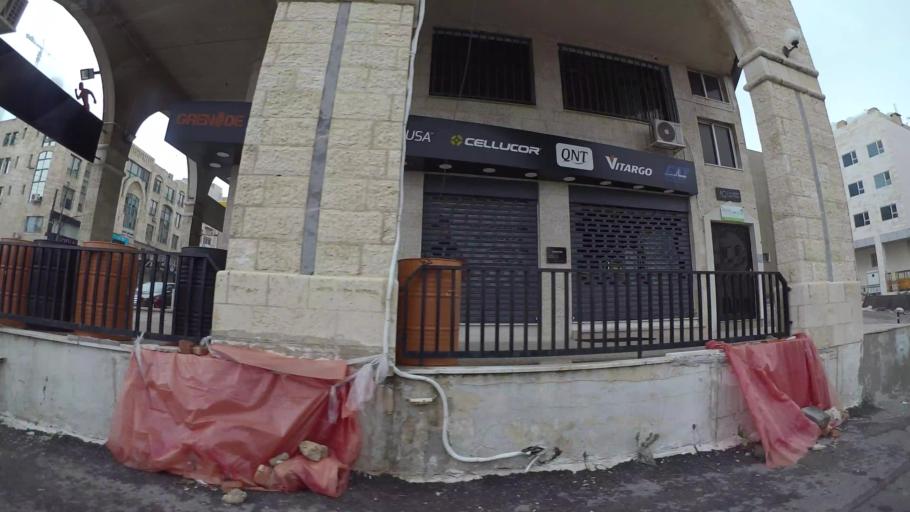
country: JO
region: Amman
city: Wadi as Sir
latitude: 31.9589
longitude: 35.8664
